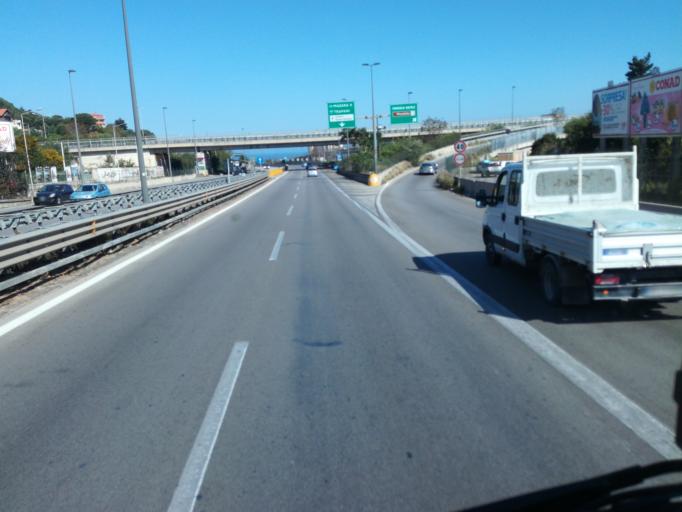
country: IT
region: Sicily
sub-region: Palermo
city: Isola delle Femmine
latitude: 38.1894
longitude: 13.2830
